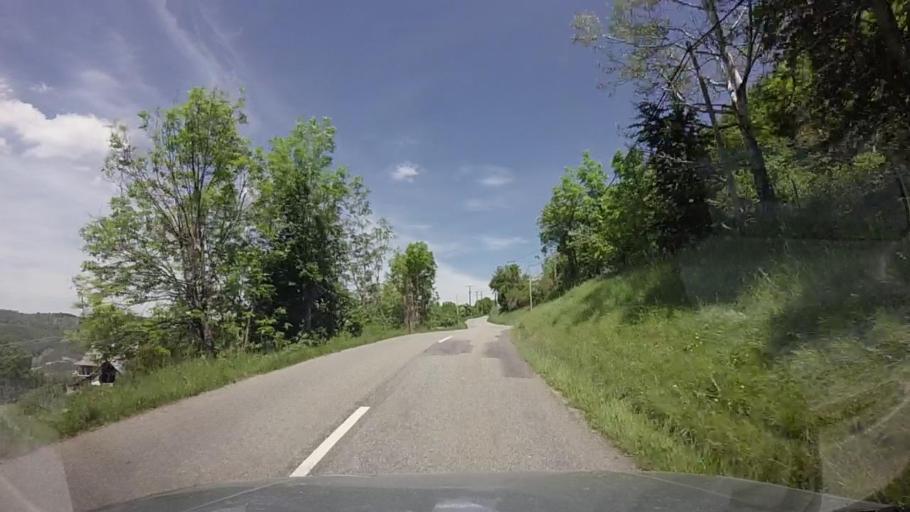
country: FR
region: Provence-Alpes-Cote d'Azur
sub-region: Departement des Alpes-de-Haute-Provence
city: Seyne-les-Alpes
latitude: 44.3955
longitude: 6.3495
